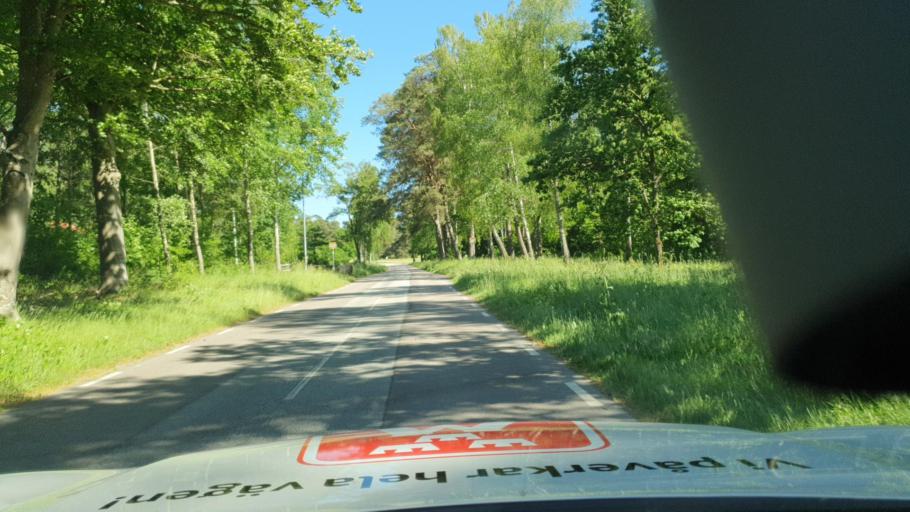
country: SE
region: Skane
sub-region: Hoors Kommun
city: Loberod
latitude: 55.7209
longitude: 13.4702
